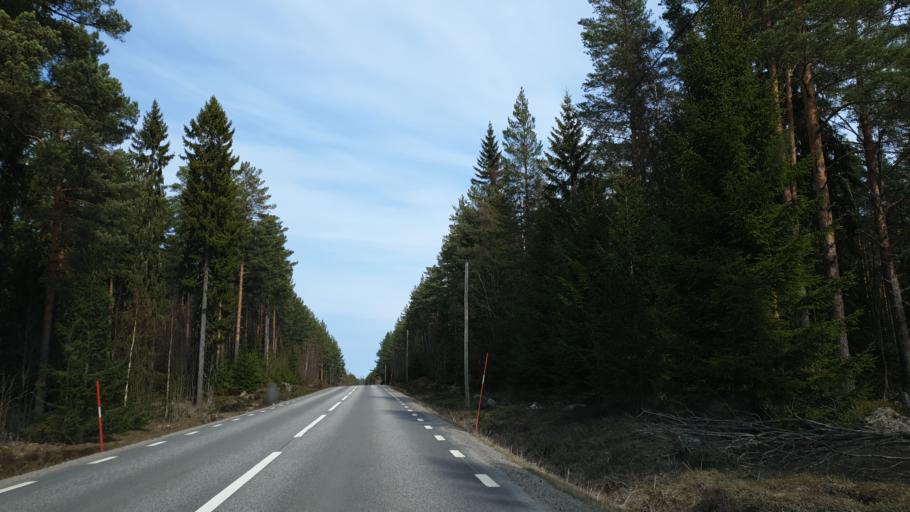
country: SE
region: Gaevleborg
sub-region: Gavle Kommun
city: Norrsundet
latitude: 61.0070
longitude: 17.1306
